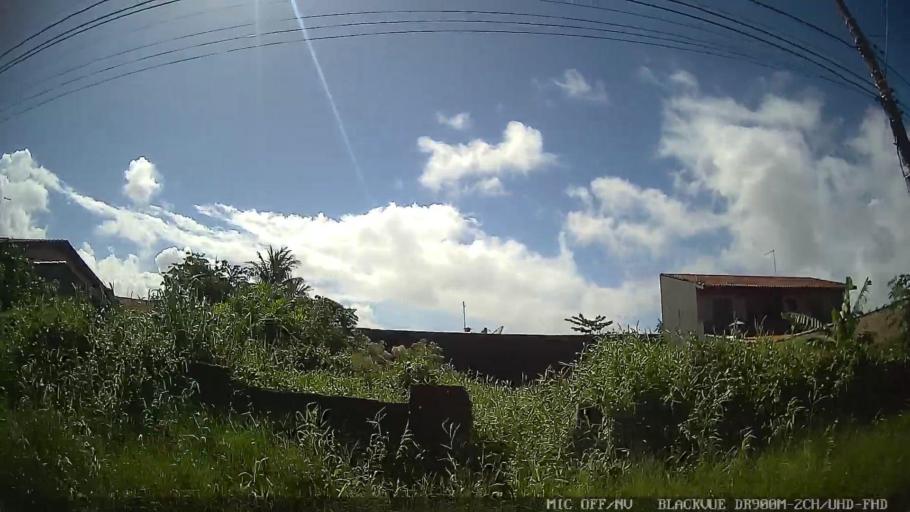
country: BR
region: Sao Paulo
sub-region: Itanhaem
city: Itanhaem
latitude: -24.2280
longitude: -46.8684
